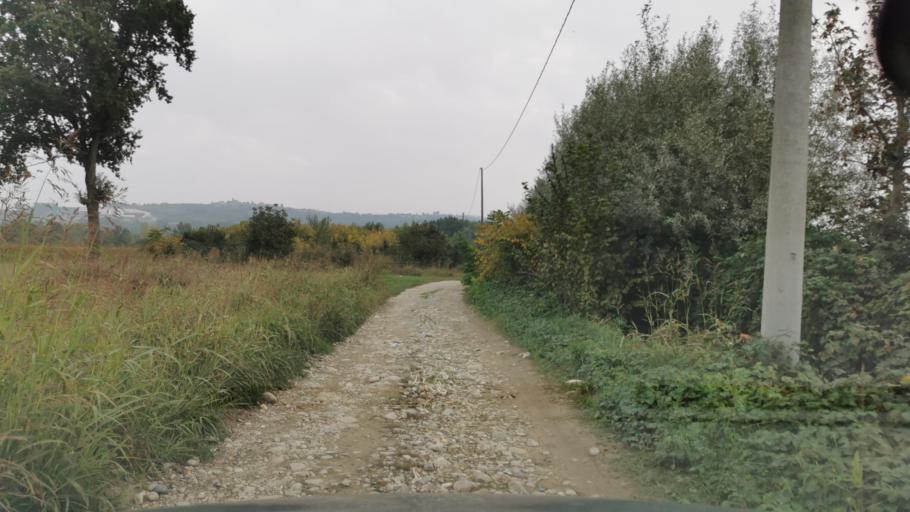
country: IT
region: Piedmont
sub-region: Provincia di Cuneo
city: Cinzano
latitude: 44.6903
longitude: 7.9126
